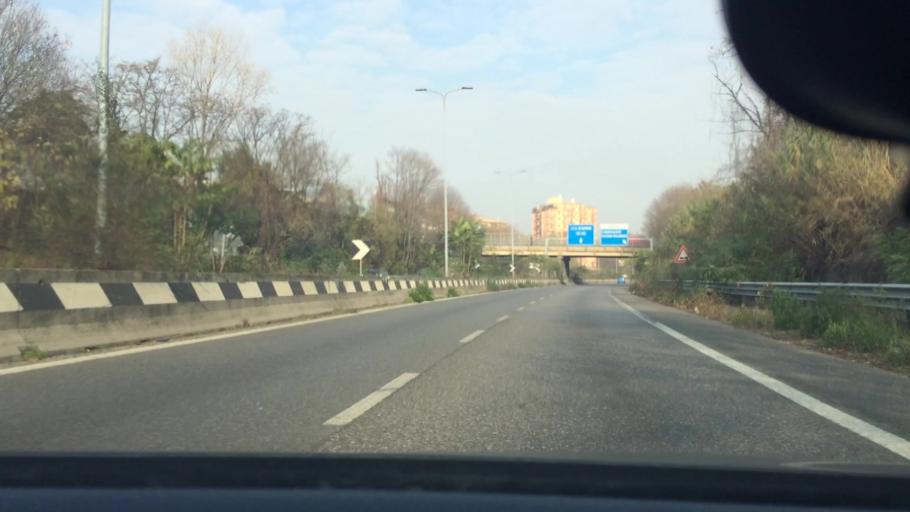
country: IT
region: Lombardy
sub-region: Citta metropolitana di Milano
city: Cormano
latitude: 45.5429
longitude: 9.1617
